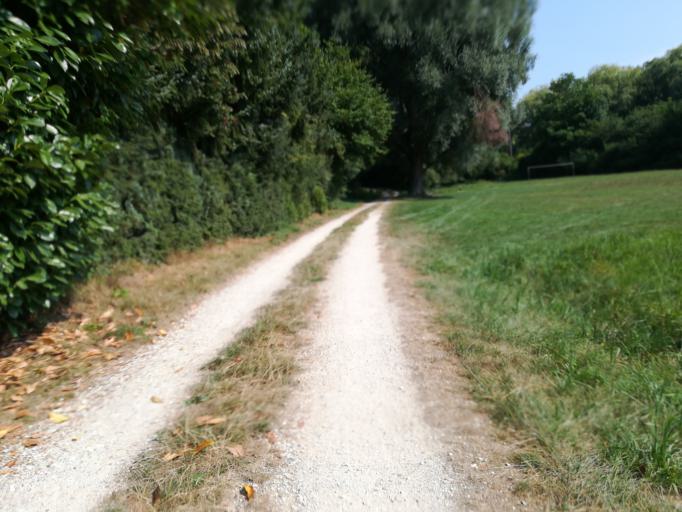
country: DE
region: Baden-Wuerttemberg
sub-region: Freiburg Region
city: Singen
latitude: 47.7646
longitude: 8.8260
